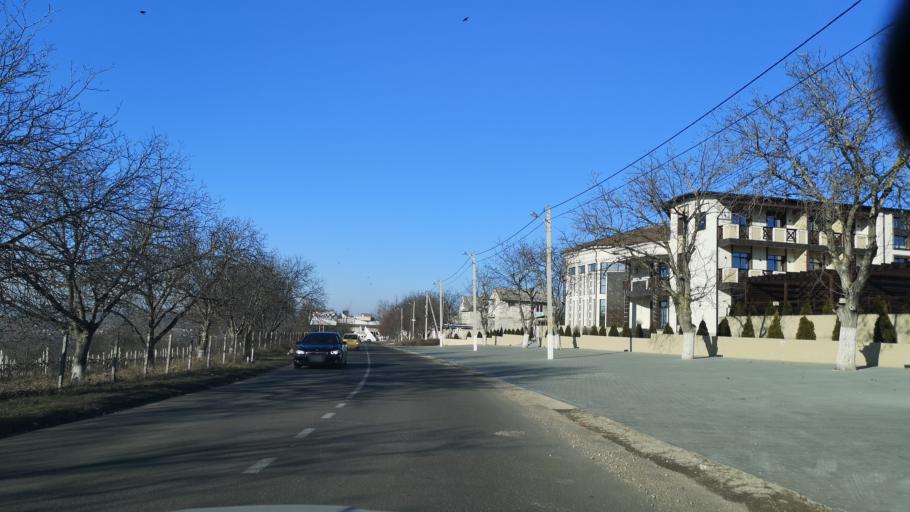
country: MD
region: Chisinau
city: Cricova
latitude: 47.1344
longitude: 28.8572
